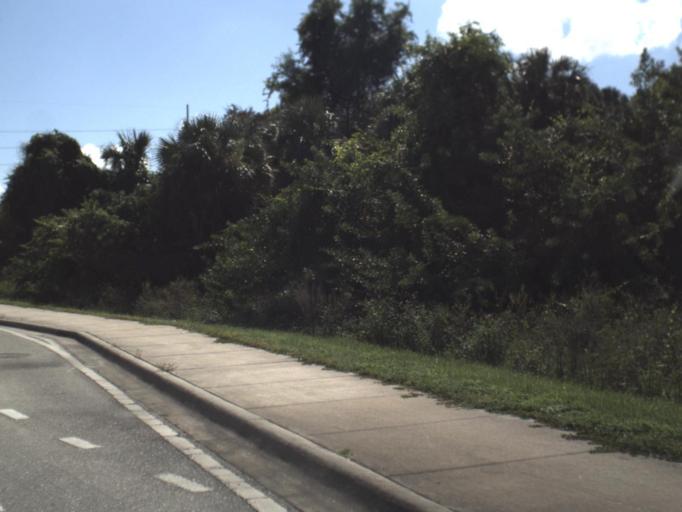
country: US
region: Florida
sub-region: Lee County
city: Palmona Park
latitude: 26.6978
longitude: -81.9420
